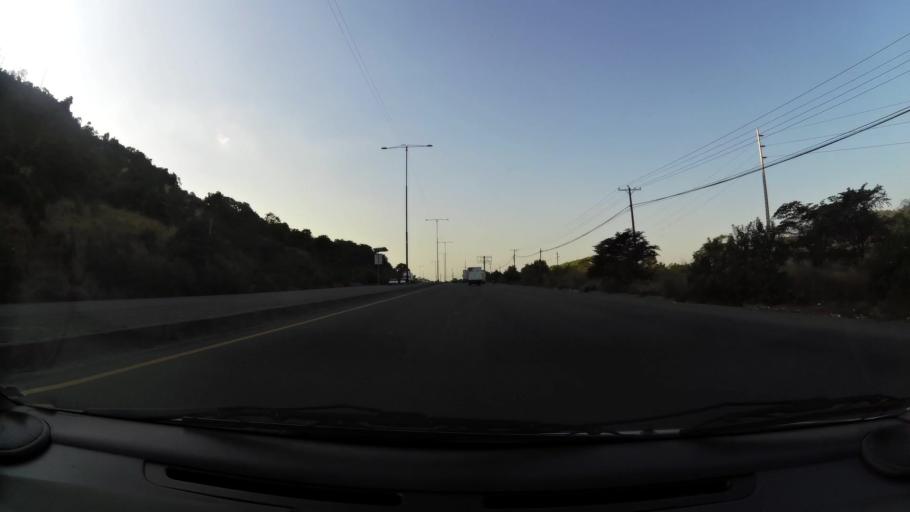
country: EC
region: Guayas
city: Guayaquil
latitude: -2.1783
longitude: -79.9463
